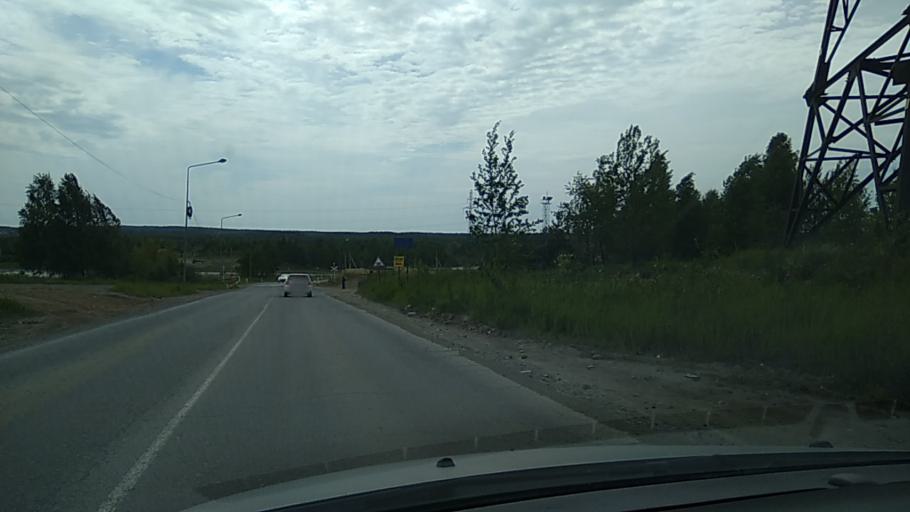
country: RU
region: Sverdlovsk
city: Verkhnyaya Pyshma
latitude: 56.9544
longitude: 60.5864
